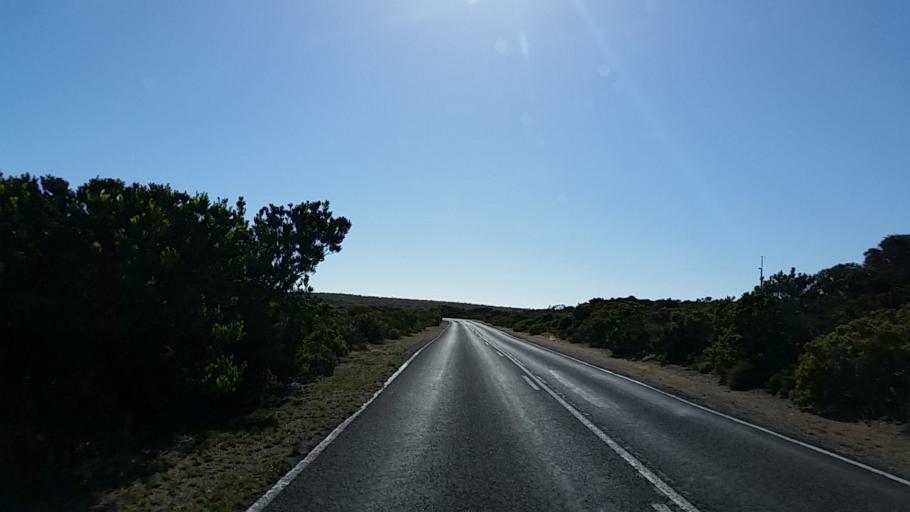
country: AU
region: South Australia
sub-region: Yorke Peninsula
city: Honiton
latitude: -35.2665
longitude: 136.9463
